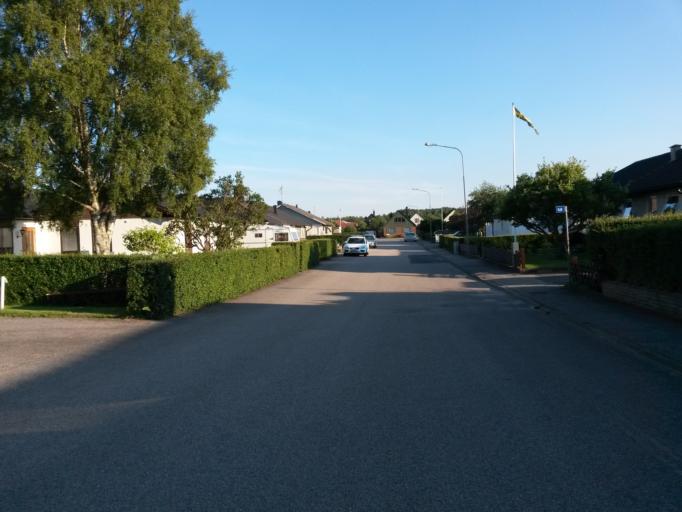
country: SE
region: Vaestra Goetaland
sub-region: Vargarda Kommun
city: Vargarda
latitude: 58.0243
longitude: 12.8120
